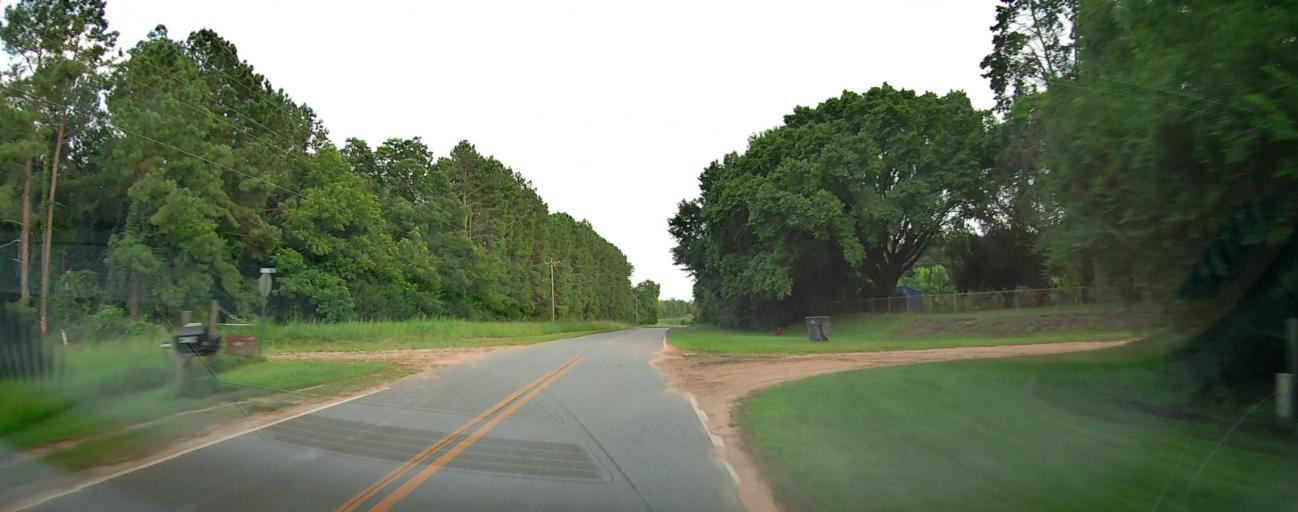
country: US
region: Georgia
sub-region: Crawford County
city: Roberta
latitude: 32.6647
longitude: -84.0662
